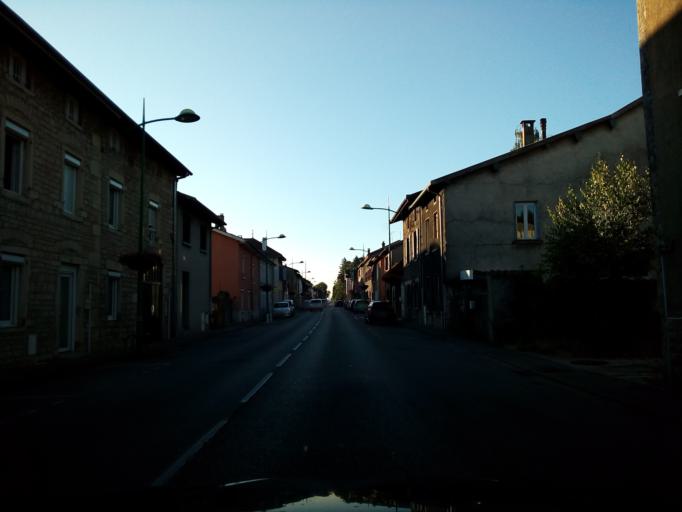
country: FR
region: Rhone-Alpes
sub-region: Departement de l'Isere
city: La Verpilliere
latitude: 45.6318
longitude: 5.1500
